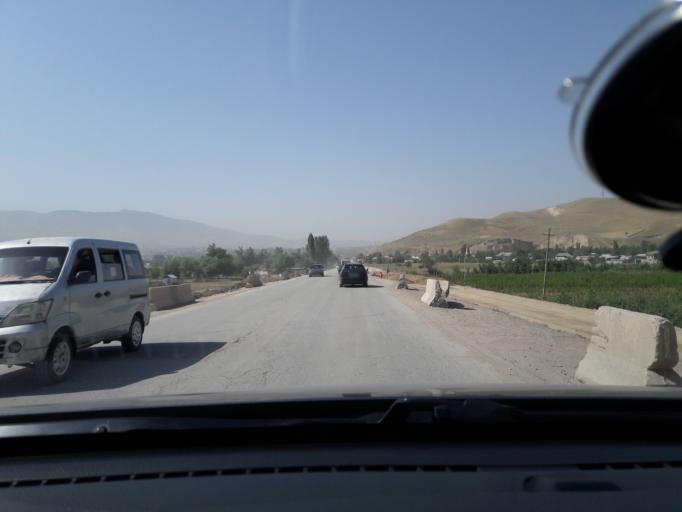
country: TJ
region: Dushanbe
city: Boshkengash
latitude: 38.4512
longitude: 68.7347
